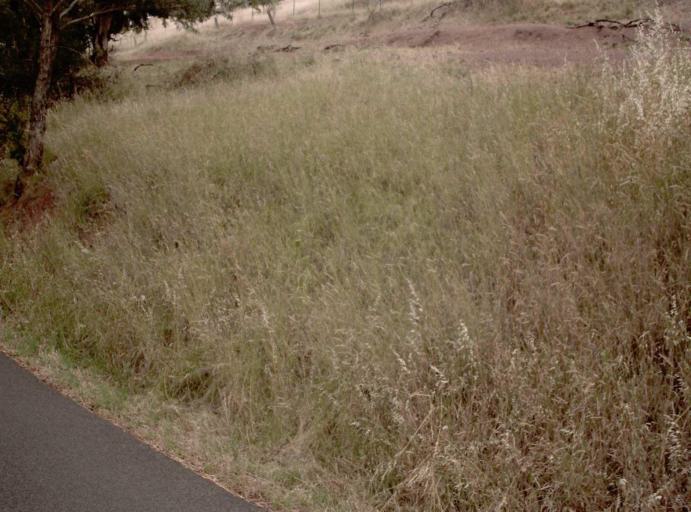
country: AU
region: Victoria
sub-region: Wellington
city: Heyfield
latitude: -37.6677
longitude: 146.6467
